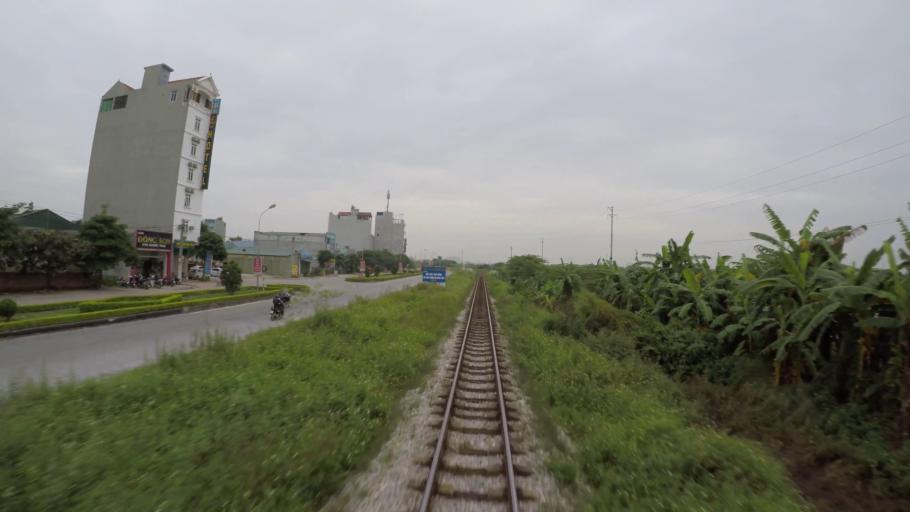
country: VN
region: Hung Yen
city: Nhu Quynh
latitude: 20.9824
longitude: 106.0284
